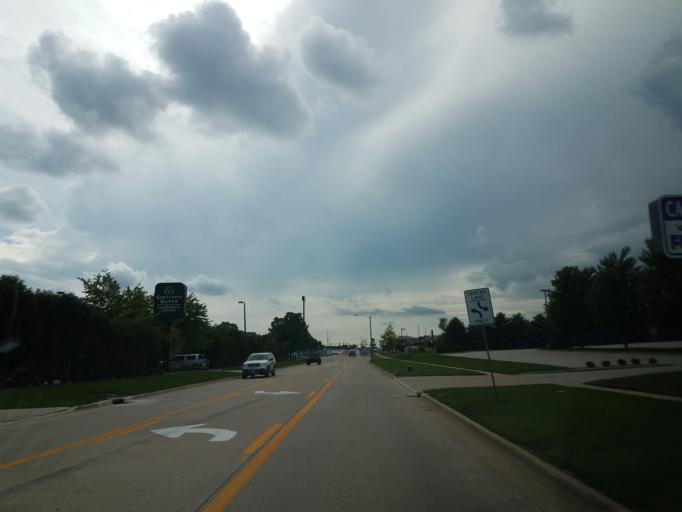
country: US
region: Illinois
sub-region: McLean County
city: Bloomington
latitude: 40.4841
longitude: -88.9472
